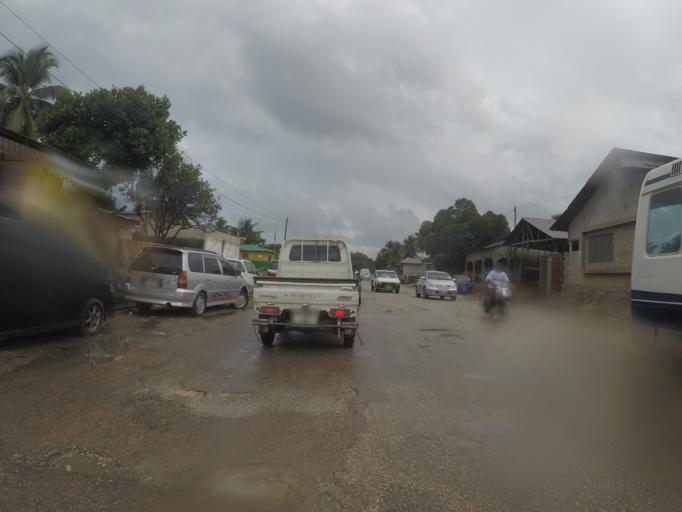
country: TZ
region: Zanzibar Urban/West
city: Zanzibar
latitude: -6.0972
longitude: 39.2191
